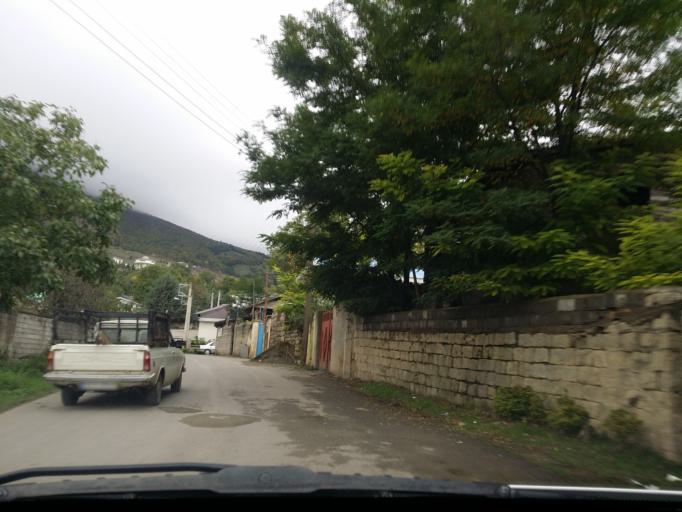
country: IR
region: Mazandaran
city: `Abbasabad
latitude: 36.5068
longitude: 51.1934
